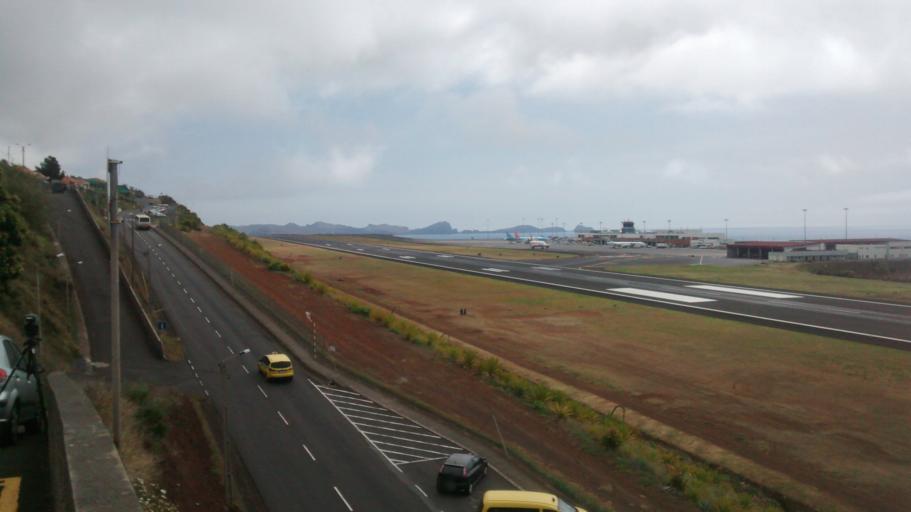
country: PT
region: Madeira
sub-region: Santa Cruz
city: Santa Cruz
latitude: 32.6915
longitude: -16.7839
